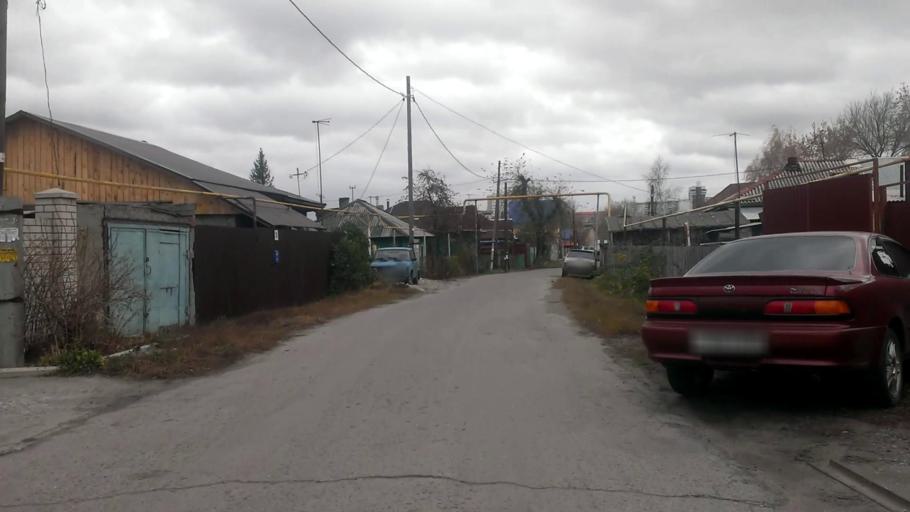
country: RU
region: Altai Krai
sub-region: Gorod Barnaulskiy
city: Barnaul
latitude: 53.3520
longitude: 83.7462
